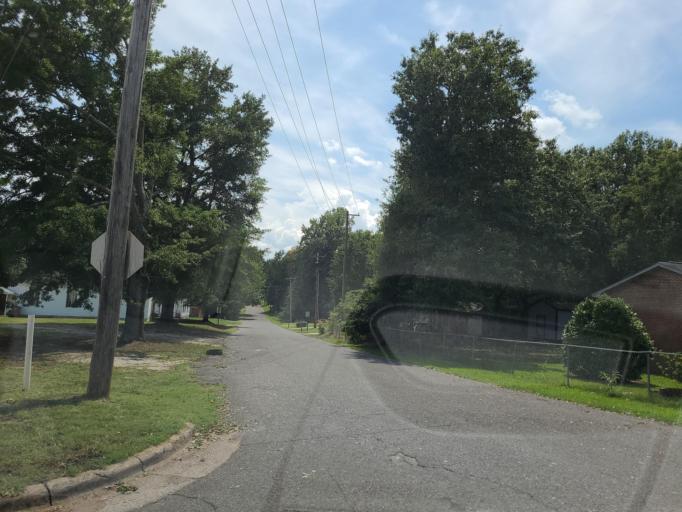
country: US
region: North Carolina
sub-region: Cleveland County
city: Shelby
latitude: 35.2745
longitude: -81.5406
